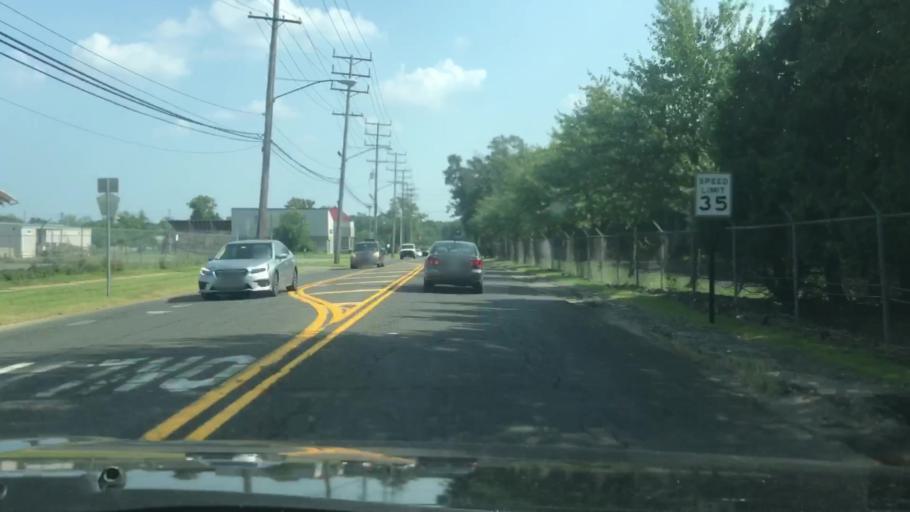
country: US
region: New Jersey
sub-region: Monmouth County
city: Oceanport
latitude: 40.3175
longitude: -74.0336
